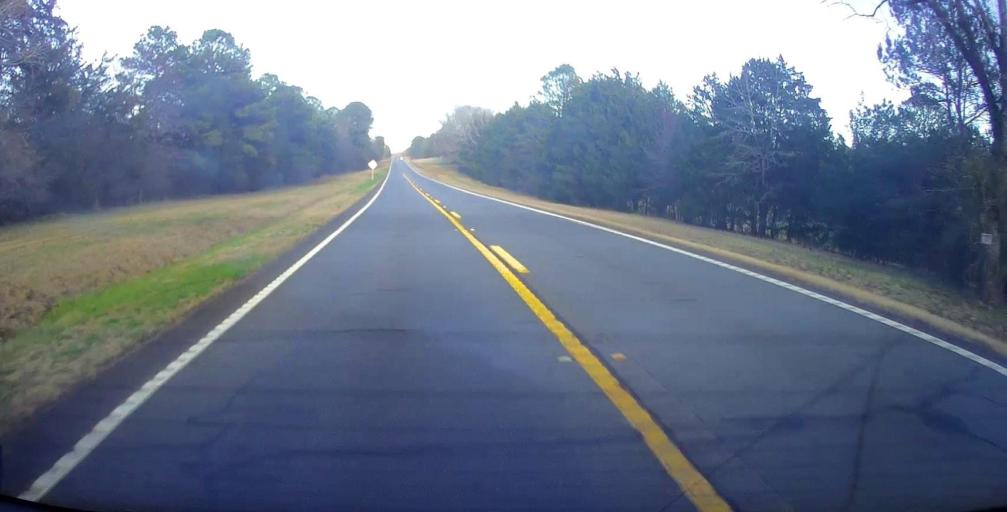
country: US
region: Georgia
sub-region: Talbot County
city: Talbotton
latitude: 32.7850
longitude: -84.5218
